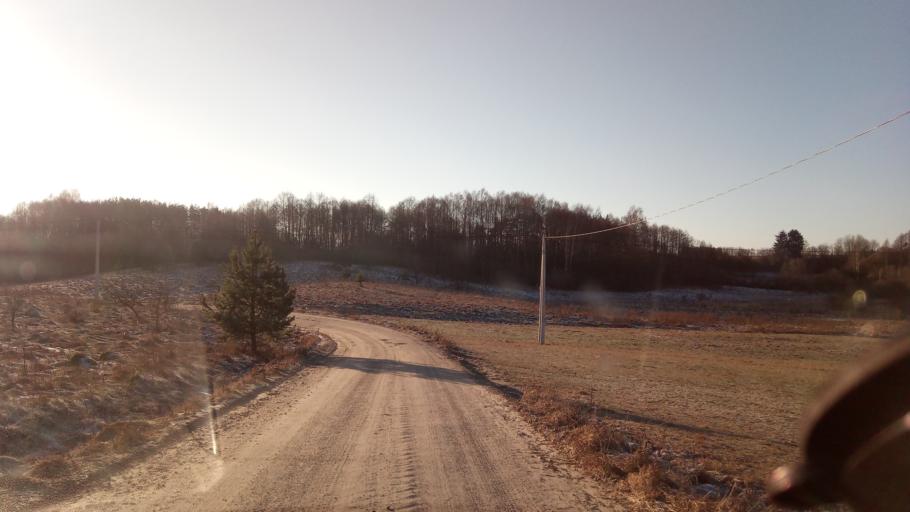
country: LT
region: Alytaus apskritis
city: Druskininkai
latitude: 54.1059
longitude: 24.0118
